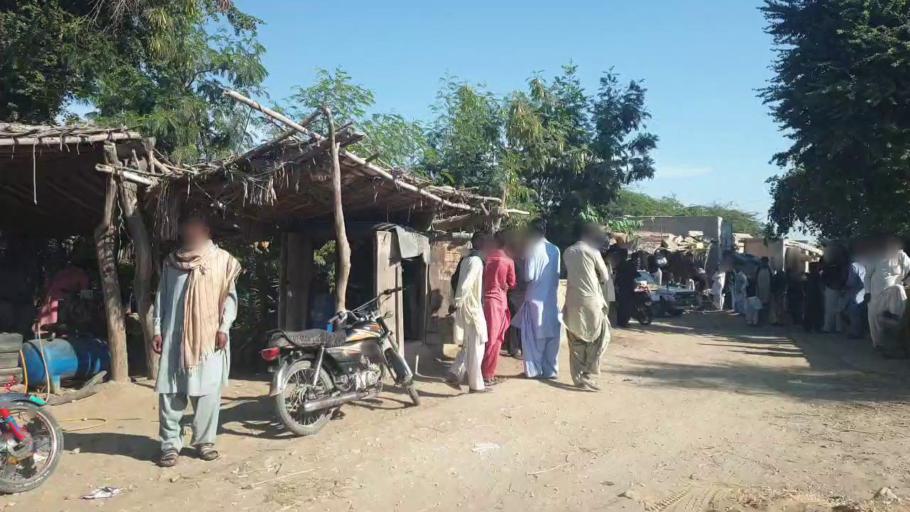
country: PK
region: Sindh
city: Rajo Khanani
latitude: 24.9714
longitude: 68.7648
